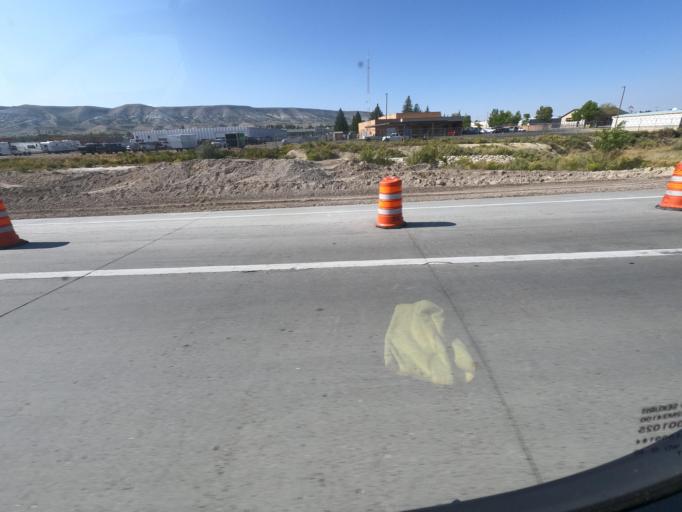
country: US
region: Wyoming
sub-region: Sweetwater County
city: Rock Springs
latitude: 41.5766
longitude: -109.2629
